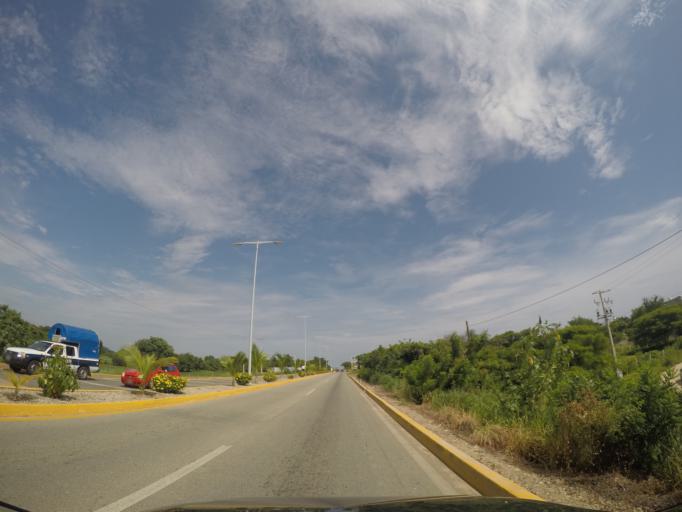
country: MX
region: Oaxaca
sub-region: Santa Maria Colotepec
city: Brisas de Zicatela
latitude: 15.8328
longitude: -97.0352
